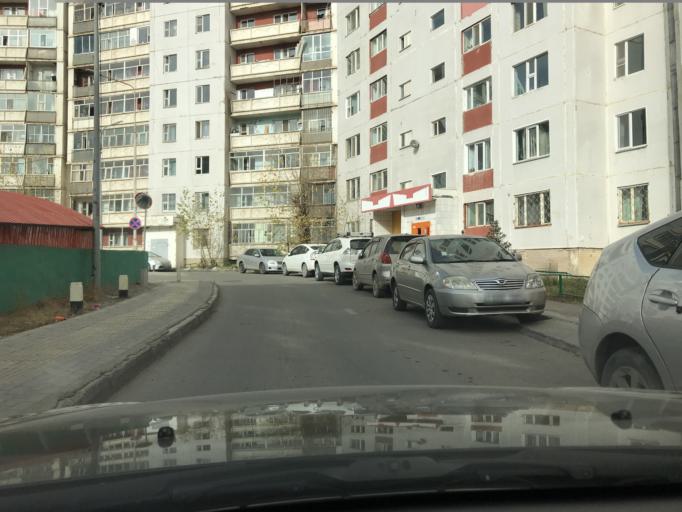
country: MN
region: Ulaanbaatar
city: Ulaanbaatar
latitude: 47.9177
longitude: 106.9411
